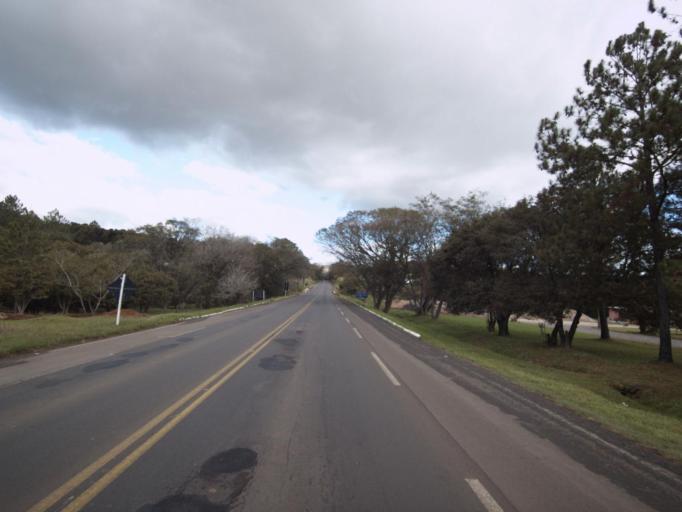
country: BR
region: Santa Catarina
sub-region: Joacaba
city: Joacaba
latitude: -27.2759
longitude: -51.4411
